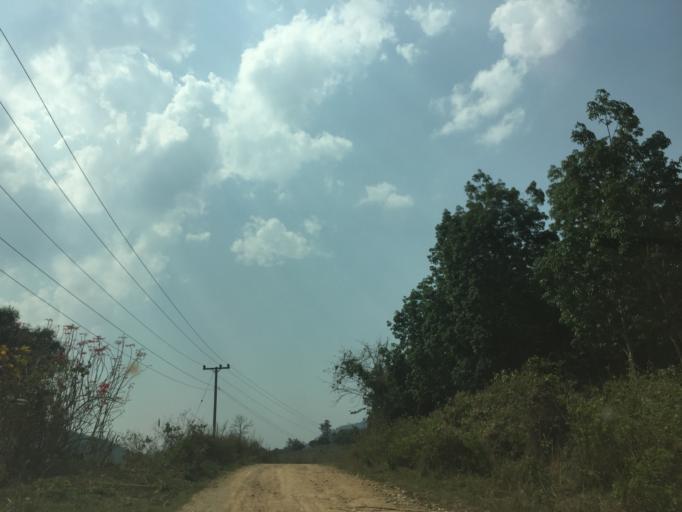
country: TH
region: Nan
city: Song Khwae
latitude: 19.7367
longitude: 100.7225
